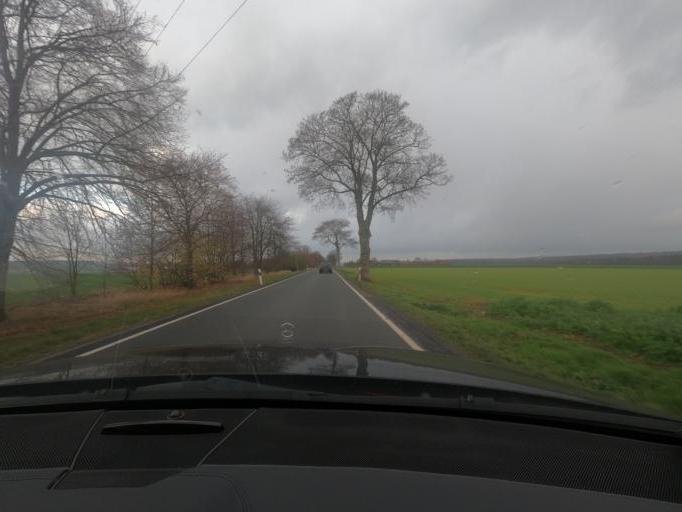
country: DE
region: North Rhine-Westphalia
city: Marsberg
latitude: 51.5524
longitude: 8.8272
